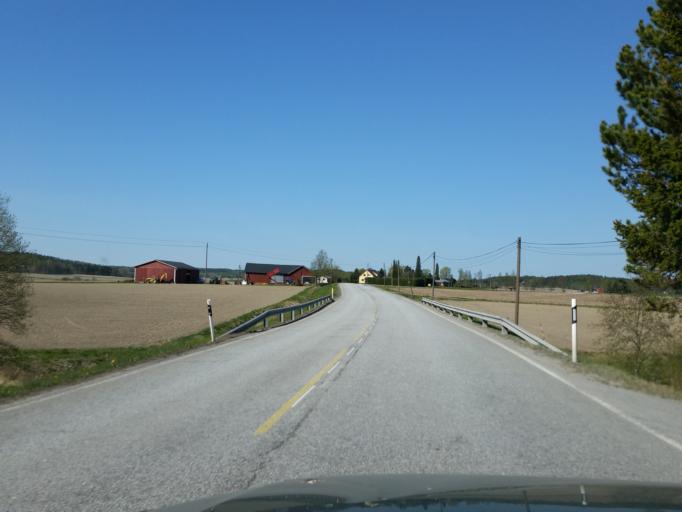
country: FI
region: Uusimaa
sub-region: Helsinki
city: Lohja
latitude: 60.1761
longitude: 24.0729
